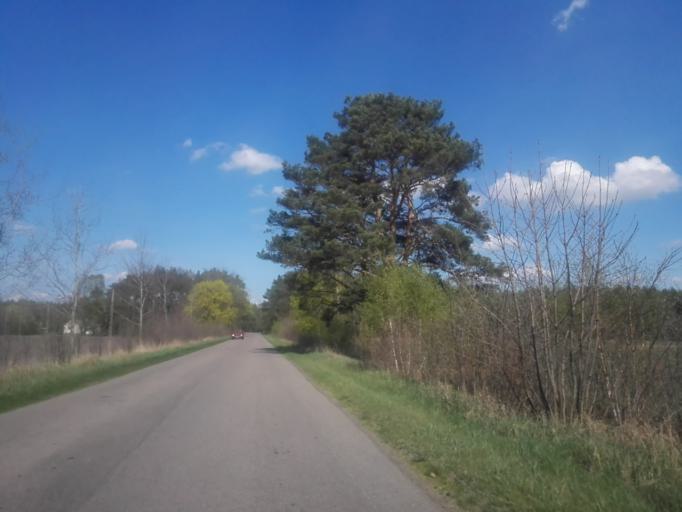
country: PL
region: Masovian Voivodeship
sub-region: Powiat sierpecki
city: Szczutowo
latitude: 52.9614
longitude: 19.6216
